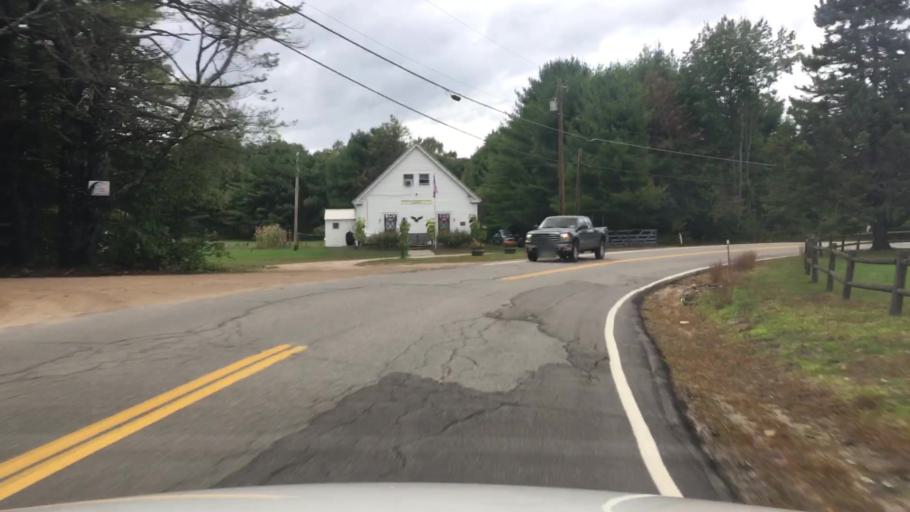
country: US
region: New Hampshire
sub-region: Carroll County
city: Effingham
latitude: 43.7371
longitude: -71.0089
